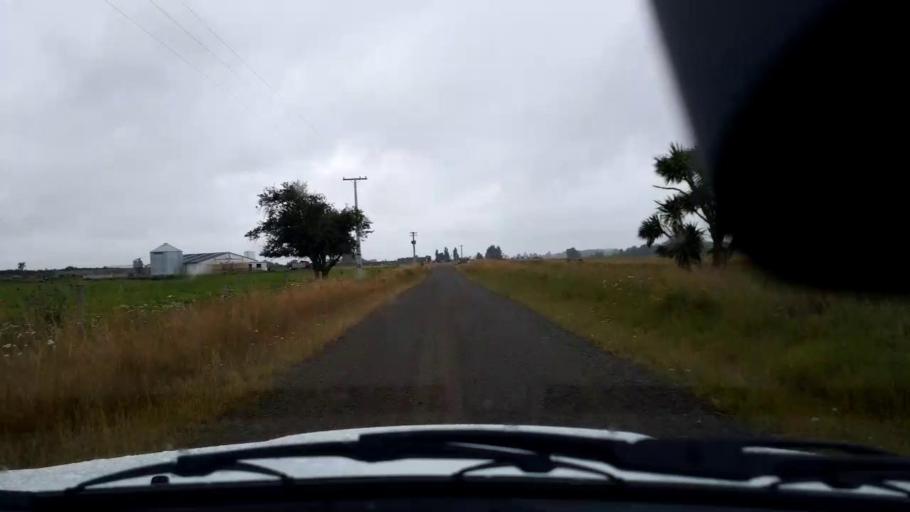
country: NZ
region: Canterbury
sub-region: Timaru District
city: Pleasant Point
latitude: -44.2534
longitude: 171.2057
